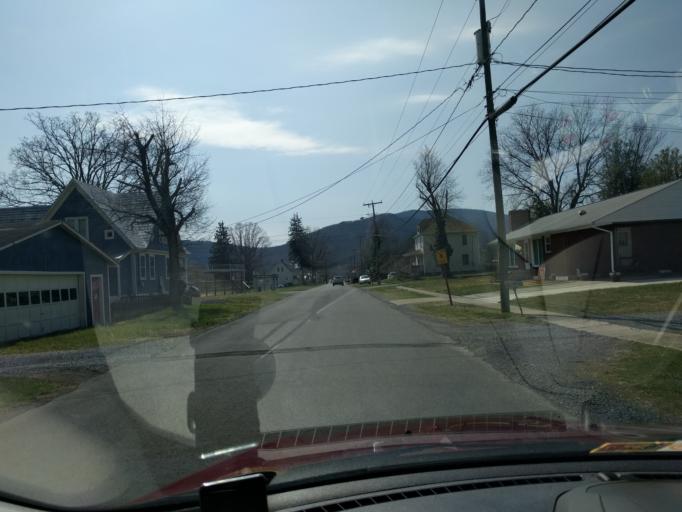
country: US
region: Virginia
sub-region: Alleghany County
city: Clifton Forge
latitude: 37.8255
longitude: -79.8213
